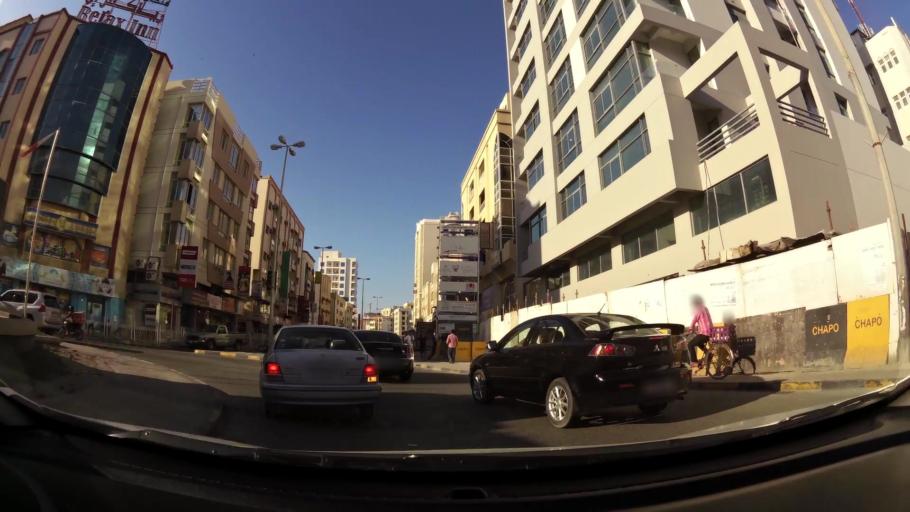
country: BH
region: Manama
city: Manama
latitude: 26.2297
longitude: 50.5954
